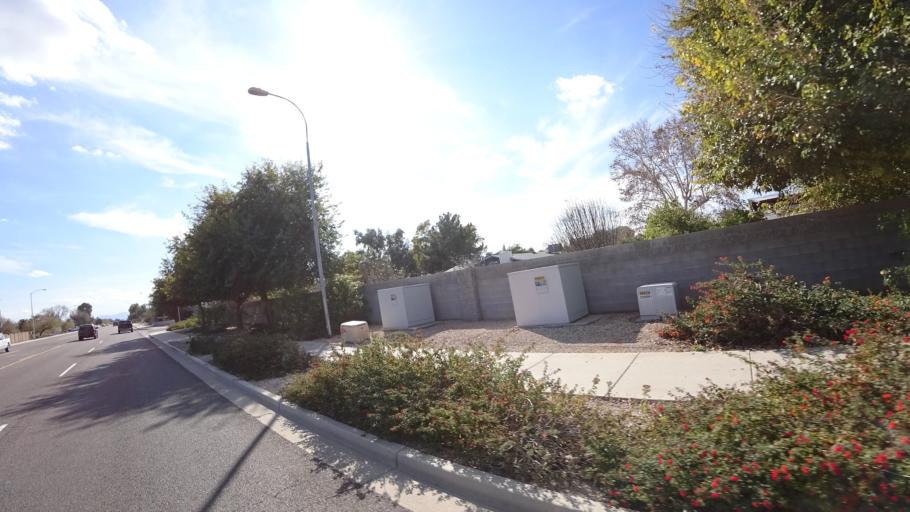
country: US
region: Arizona
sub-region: Maricopa County
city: Peoria
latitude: 33.6181
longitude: -112.2201
